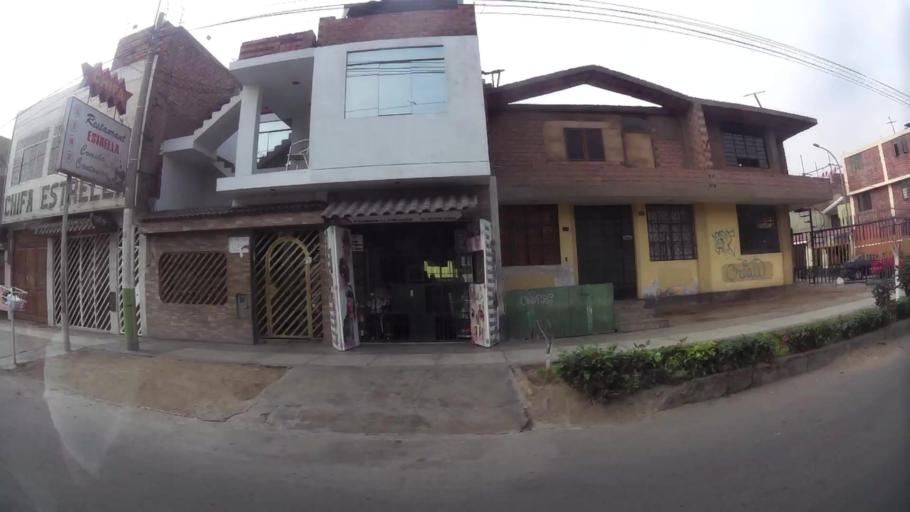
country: PE
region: Callao
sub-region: Callao
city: Callao
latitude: -12.0213
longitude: -77.0943
